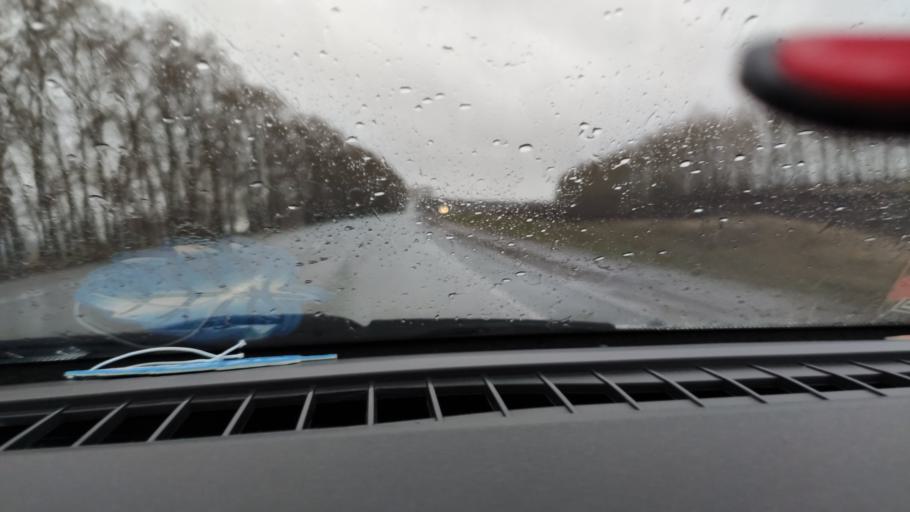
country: RU
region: Tatarstan
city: Mendeleyevsk
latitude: 55.8450
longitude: 52.2055
